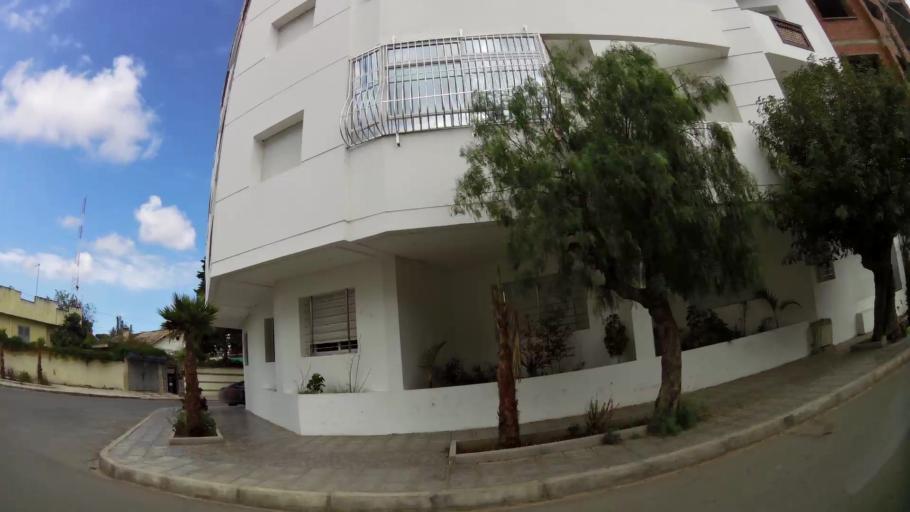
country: MA
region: Gharb-Chrarda-Beni Hssen
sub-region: Kenitra Province
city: Kenitra
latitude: 34.2539
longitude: -6.5837
